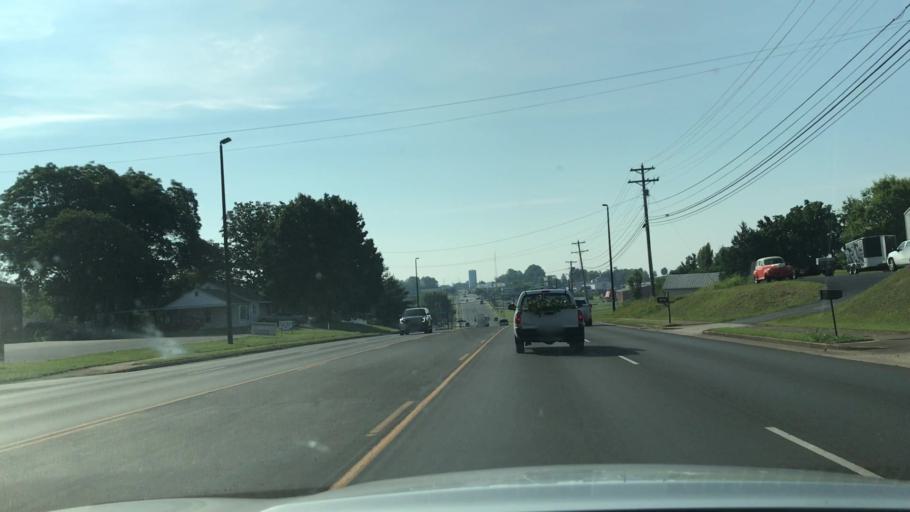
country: US
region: Kentucky
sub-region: Barren County
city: Glasgow
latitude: 37.0061
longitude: -85.9331
